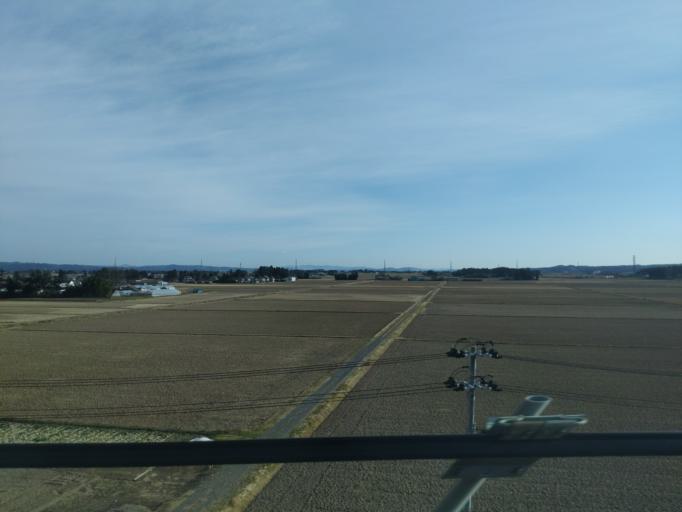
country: JP
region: Miyagi
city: Furukawa
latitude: 38.5526
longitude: 140.9631
